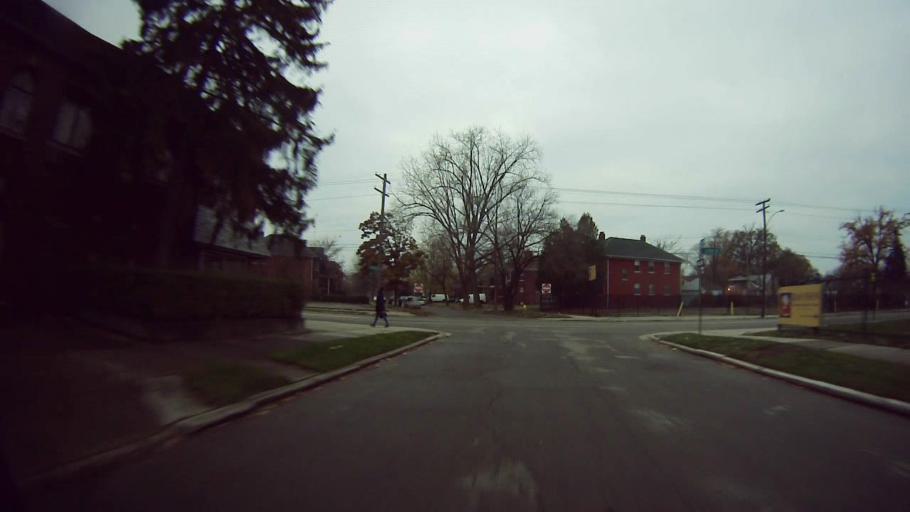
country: US
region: Michigan
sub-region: Wayne County
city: Highland Park
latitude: 42.4202
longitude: -83.1016
